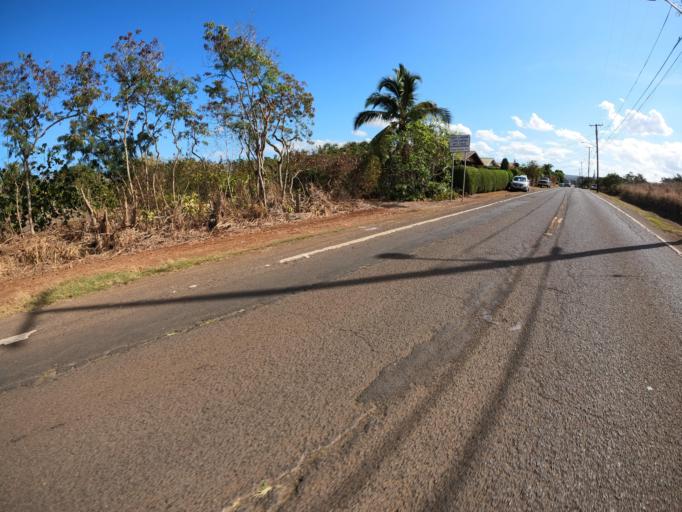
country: US
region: Hawaii
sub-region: Honolulu County
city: Waialua
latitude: 21.5691
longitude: -158.1341
